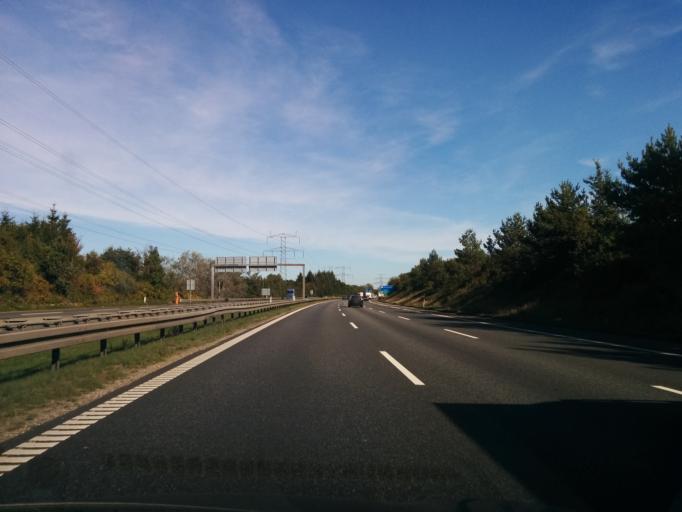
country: DK
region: South Denmark
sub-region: Kolding Kommune
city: Kolding
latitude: 55.5219
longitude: 9.4444
